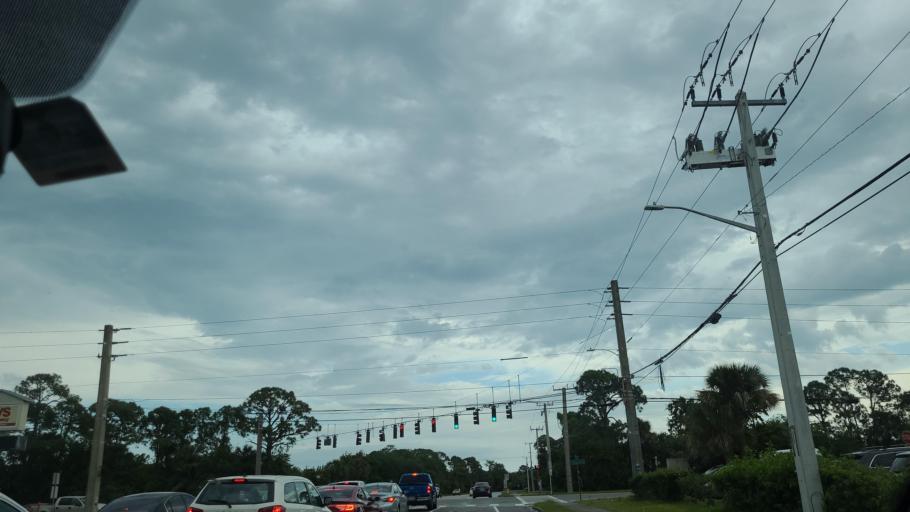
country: US
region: Florida
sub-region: Brevard County
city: June Park
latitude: 28.0322
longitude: -80.6723
